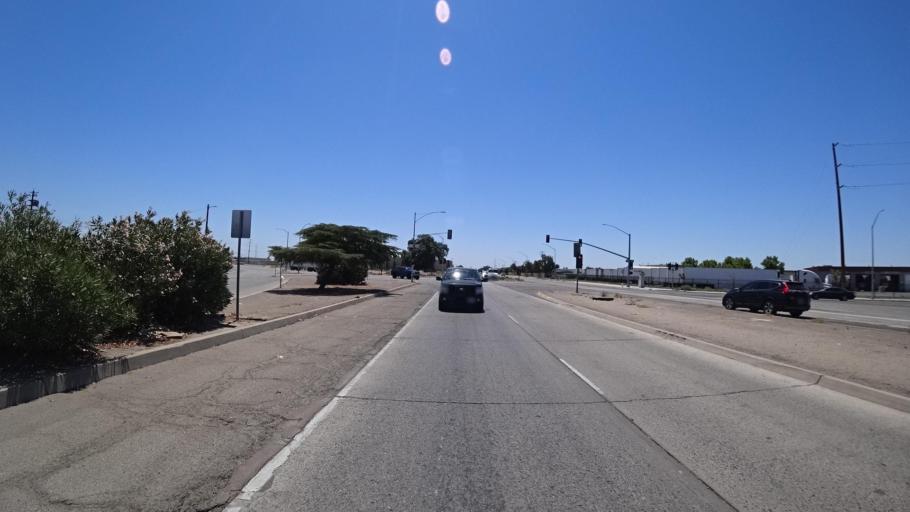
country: US
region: California
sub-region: Fresno County
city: Fresno
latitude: 36.7146
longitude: -119.7765
